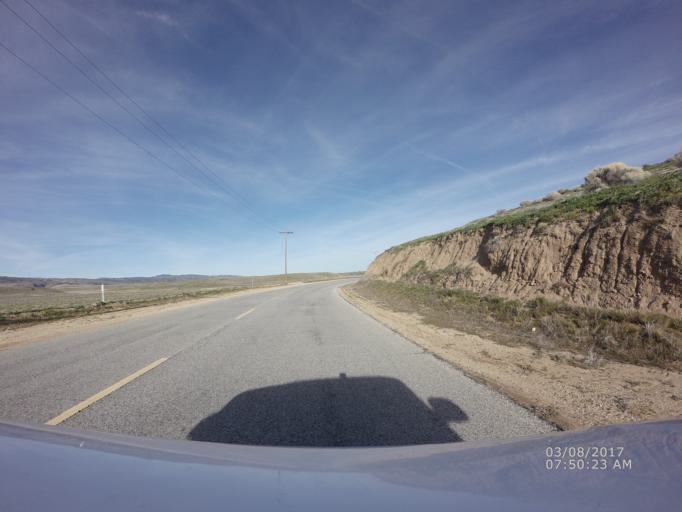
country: US
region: California
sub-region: Los Angeles County
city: Green Valley
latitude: 34.7163
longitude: -118.3638
